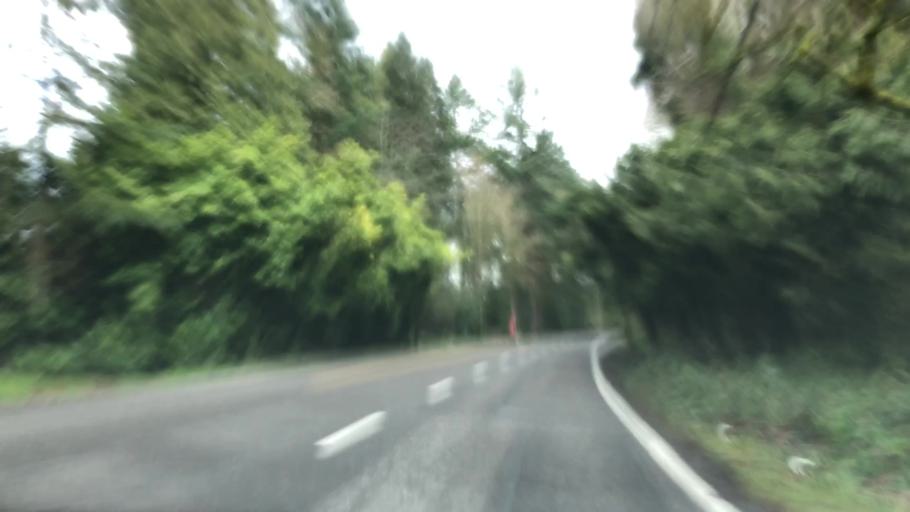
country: US
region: Oregon
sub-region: Washington County
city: West Slope
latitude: 45.4945
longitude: -122.7432
